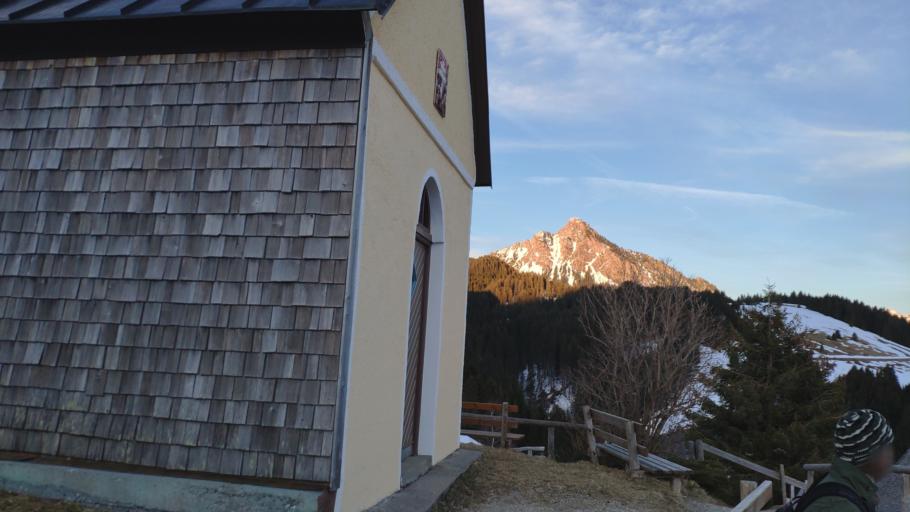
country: AT
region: Tyrol
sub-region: Politischer Bezirk Reutte
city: Zoblen
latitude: 47.5133
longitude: 10.4774
